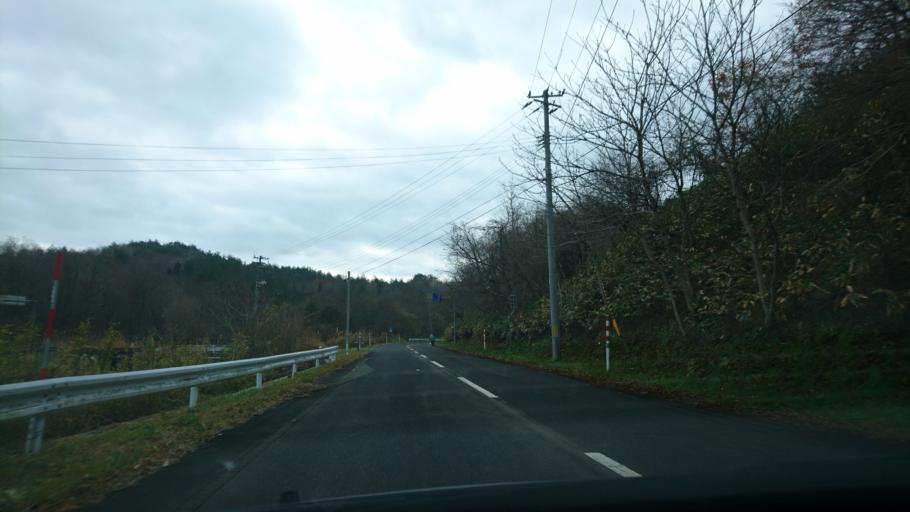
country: JP
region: Iwate
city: Ichinoseki
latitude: 38.9279
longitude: 140.9224
